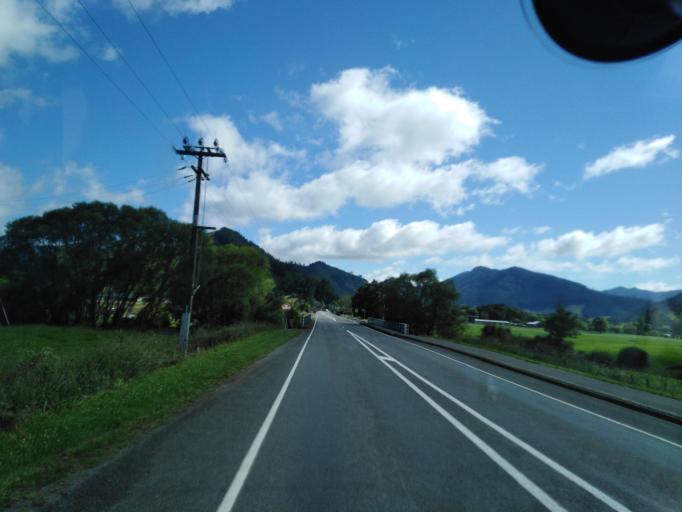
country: NZ
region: Nelson
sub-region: Nelson City
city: Nelson
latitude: -41.2331
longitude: 173.5813
